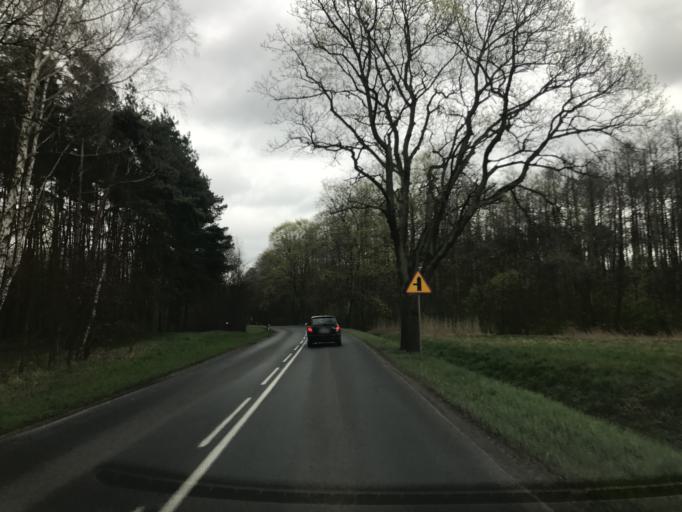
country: PL
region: Kujawsko-Pomorskie
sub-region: Bydgoszcz
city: Fordon
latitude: 53.1380
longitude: 18.1921
